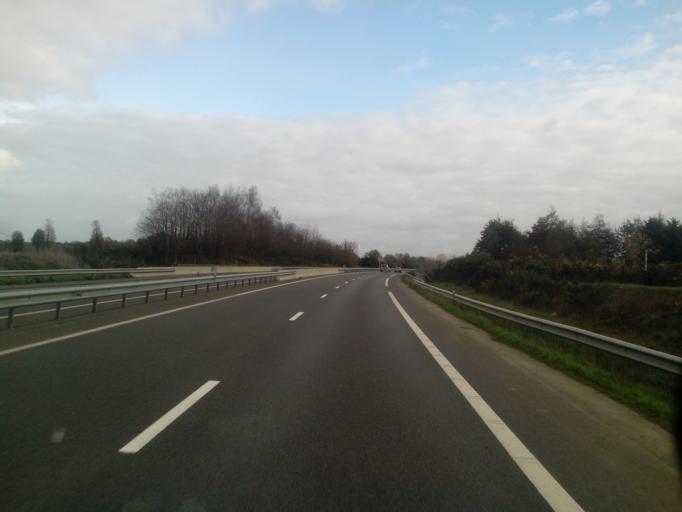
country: FR
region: Brittany
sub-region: Departement d'Ille-et-Vilaine
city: Saint-Meen-le-Grand
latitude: 48.1902
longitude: -2.1606
